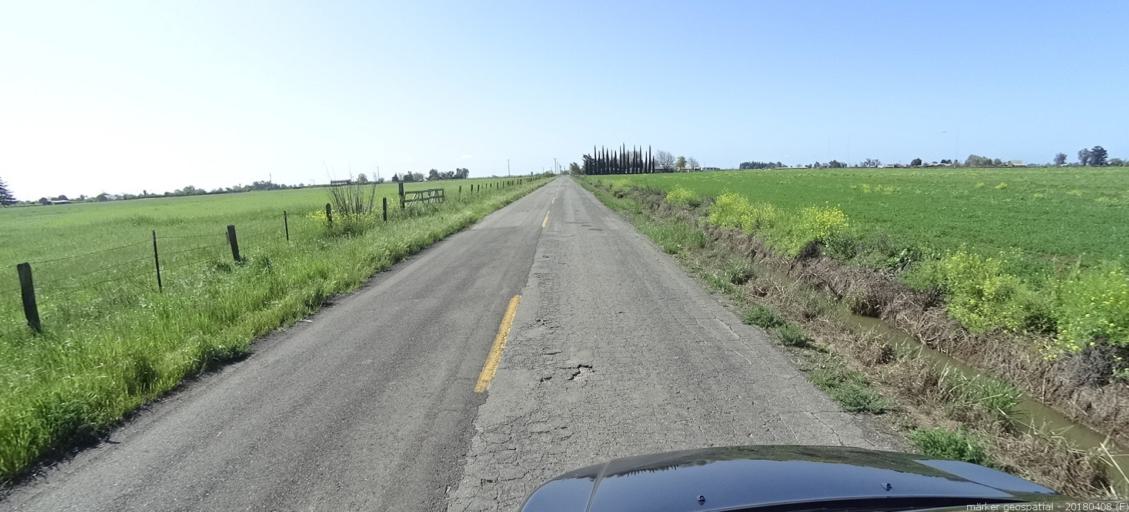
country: US
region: California
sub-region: Sacramento County
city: Laguna
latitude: 38.3460
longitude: -121.4359
